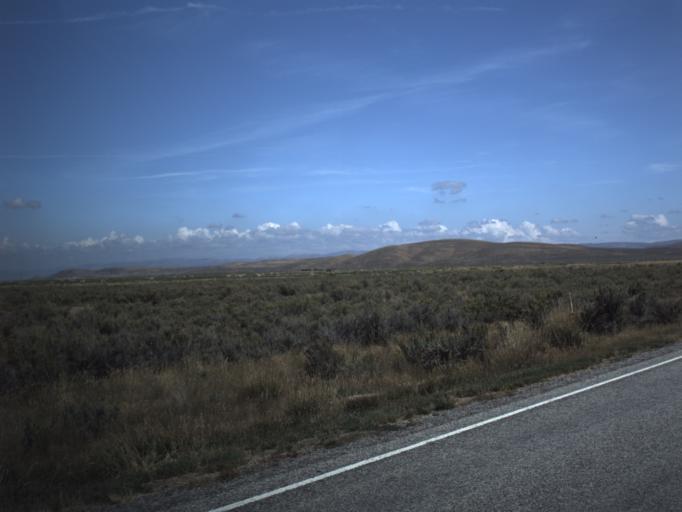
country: US
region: Utah
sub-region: Rich County
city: Randolph
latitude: 41.7779
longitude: -111.0642
